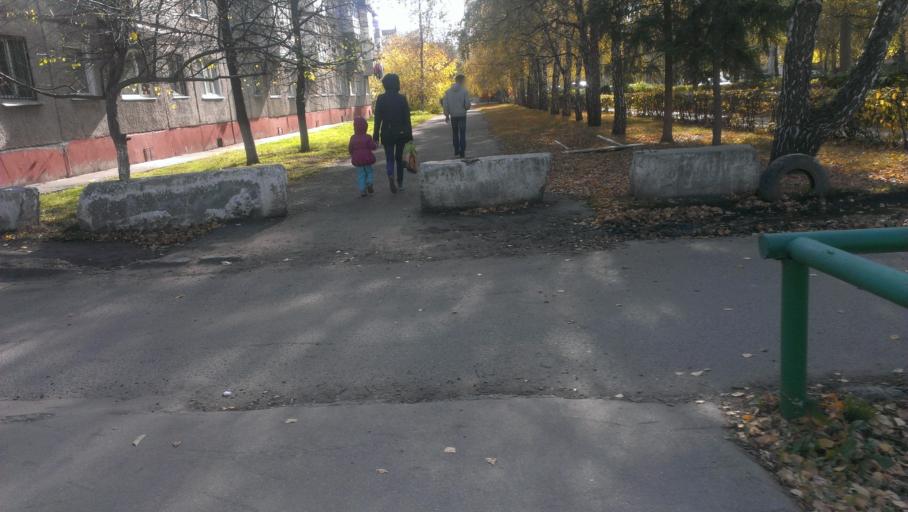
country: RU
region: Altai Krai
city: Novosilikatnyy
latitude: 53.3524
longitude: 83.6841
